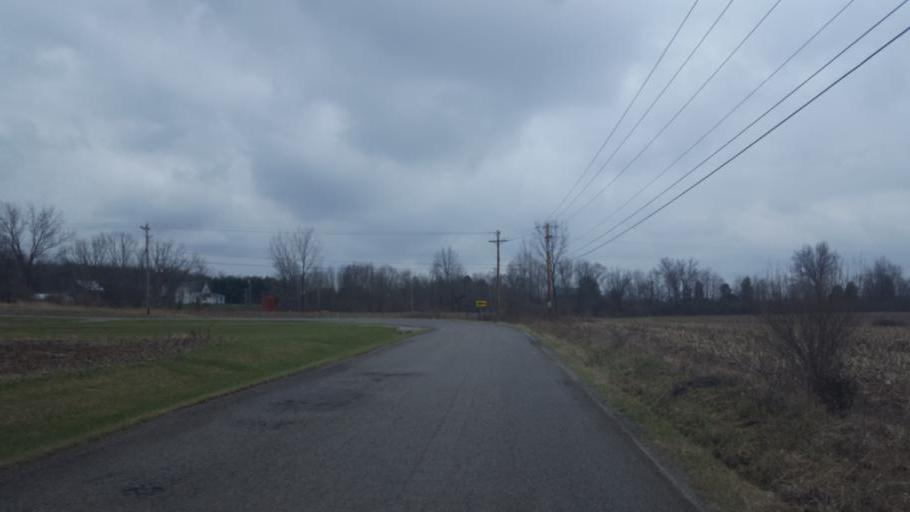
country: US
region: Ohio
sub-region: Delaware County
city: Ashley
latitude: 40.3917
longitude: -82.8534
